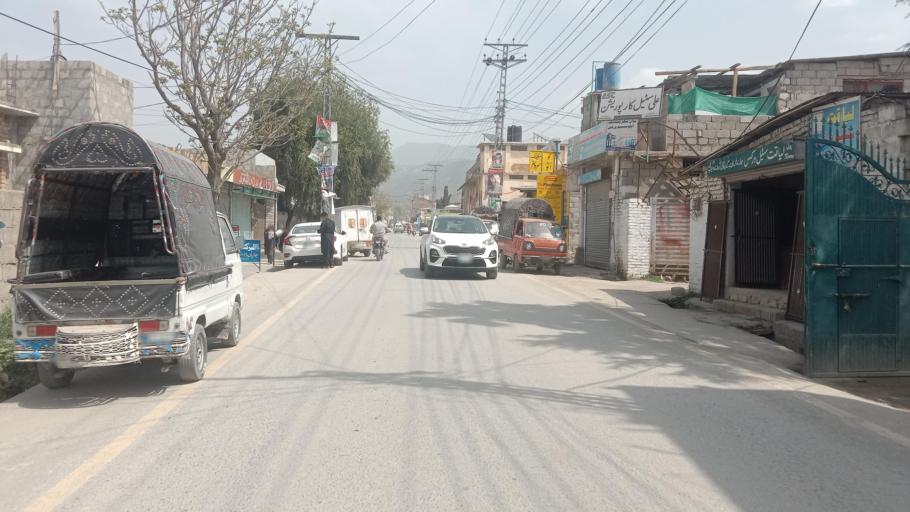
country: PK
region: Khyber Pakhtunkhwa
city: Abbottabad
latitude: 34.1623
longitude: 73.2561
